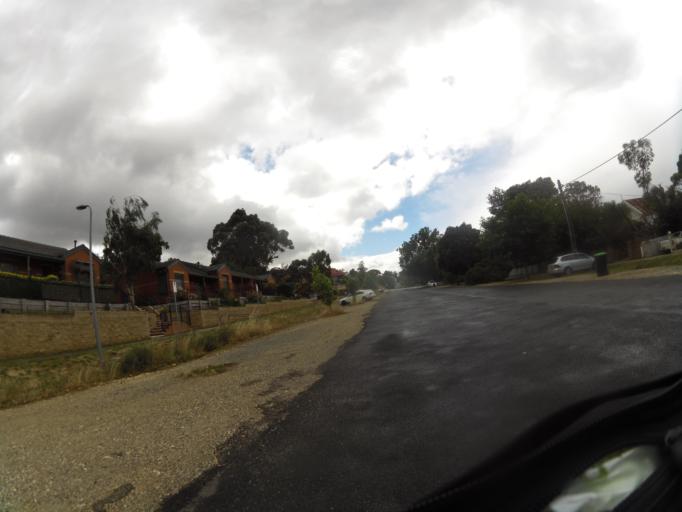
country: AU
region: Victoria
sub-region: Mount Alexander
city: Castlemaine
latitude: -37.0648
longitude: 144.2206
